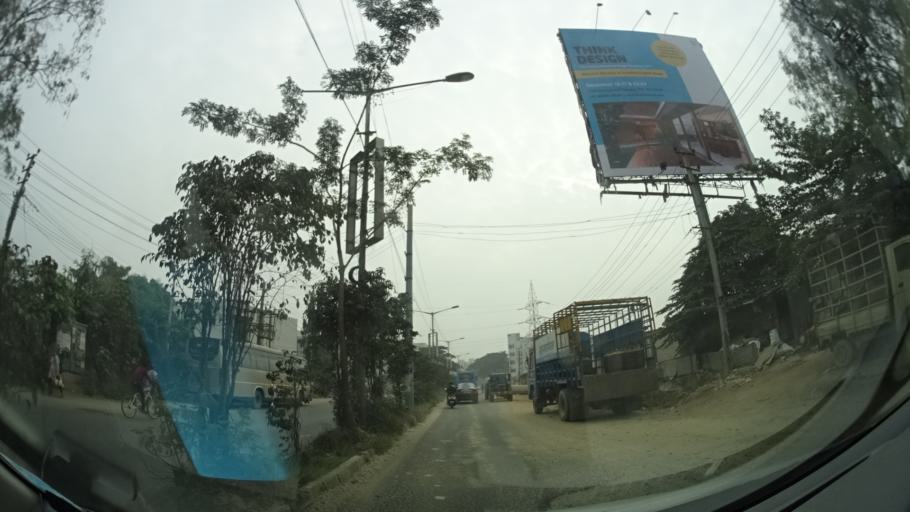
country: IN
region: Karnataka
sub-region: Bangalore Rural
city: Hoskote
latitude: 12.9926
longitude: 77.7117
